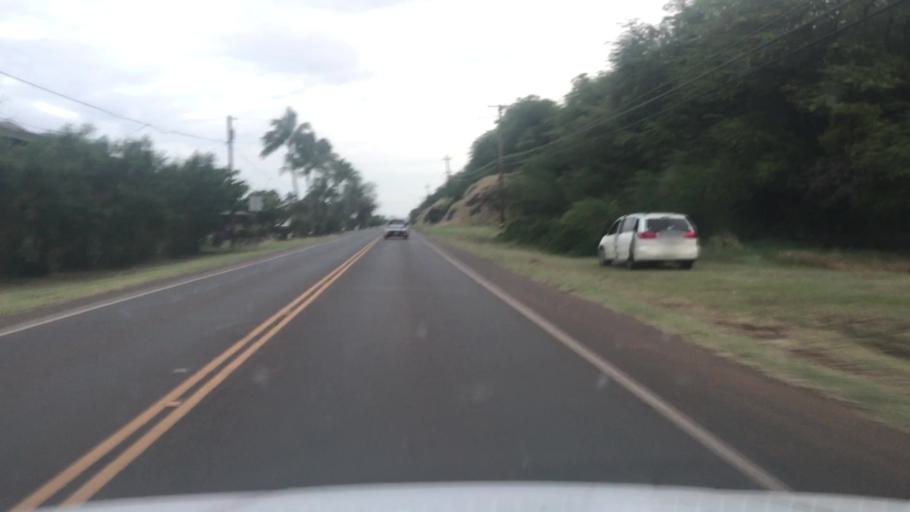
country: US
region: Hawaii
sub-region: Maui County
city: Kaunakakai
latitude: 21.0705
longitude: -156.9686
